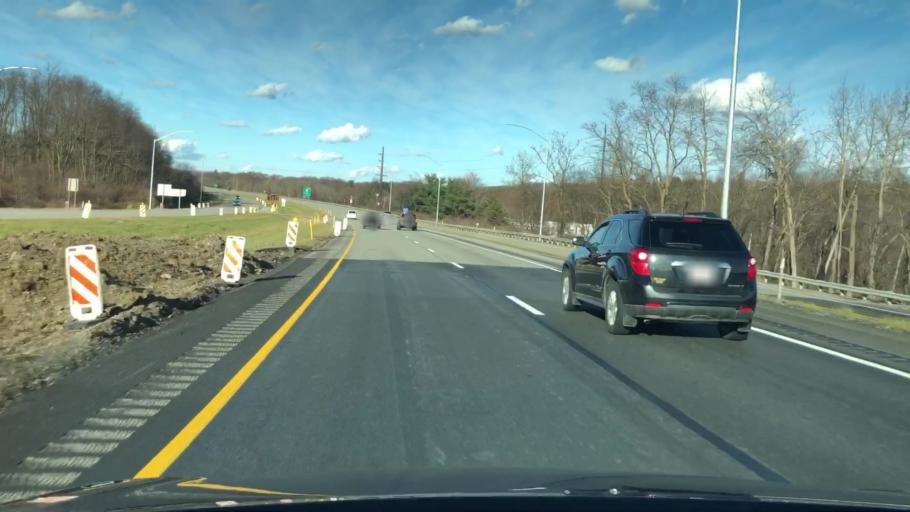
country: US
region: Pennsylvania
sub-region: Armstrong County
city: Freeport
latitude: 40.6698
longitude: -79.7142
